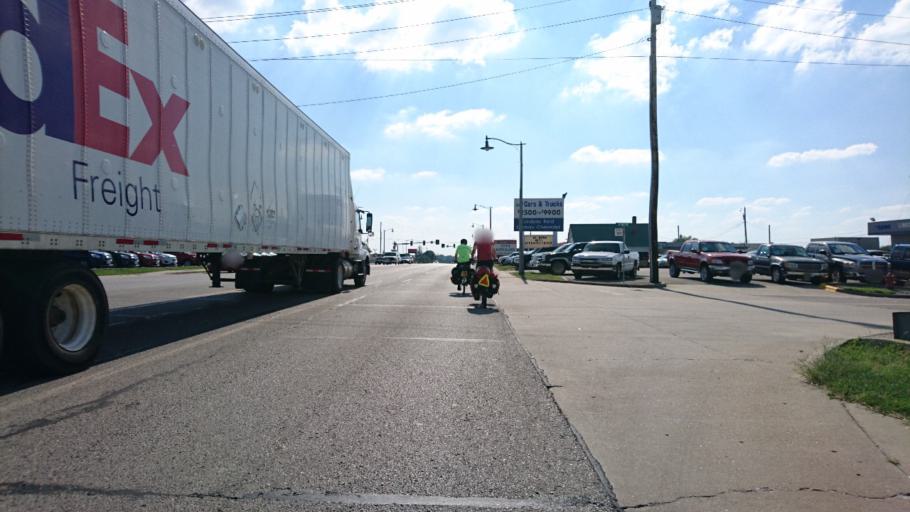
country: US
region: Missouri
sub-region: Laclede County
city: Lebanon
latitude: 37.6746
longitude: -92.6602
